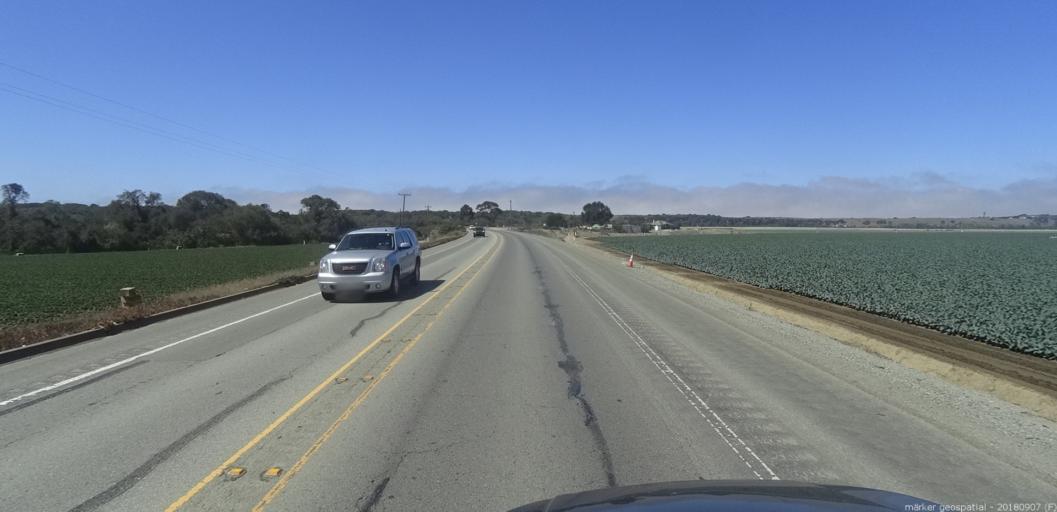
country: US
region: California
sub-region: Monterey County
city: Marina
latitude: 36.6786
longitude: -121.7407
